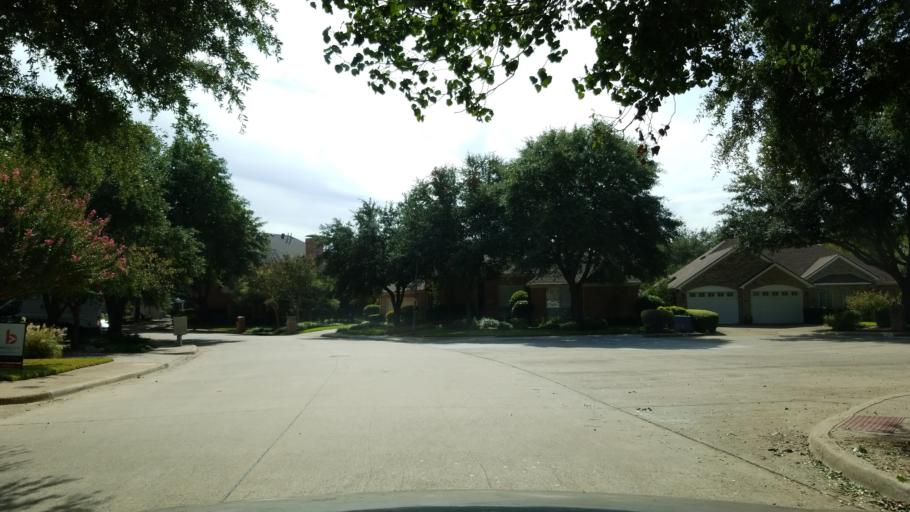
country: US
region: Texas
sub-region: Dallas County
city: Highland Park
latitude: 32.8102
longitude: -96.7239
